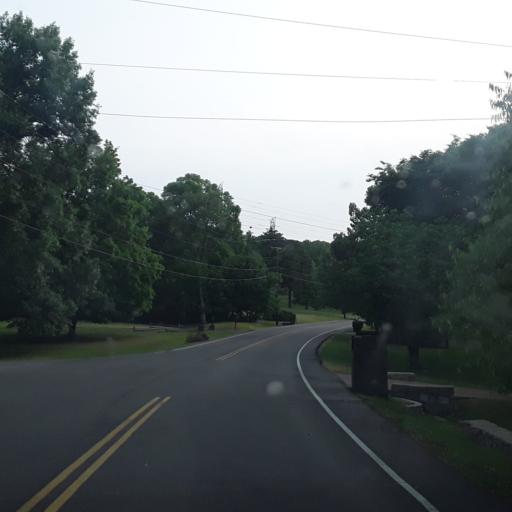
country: US
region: Tennessee
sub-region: Williamson County
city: Brentwood
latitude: 36.0523
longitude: -86.7816
